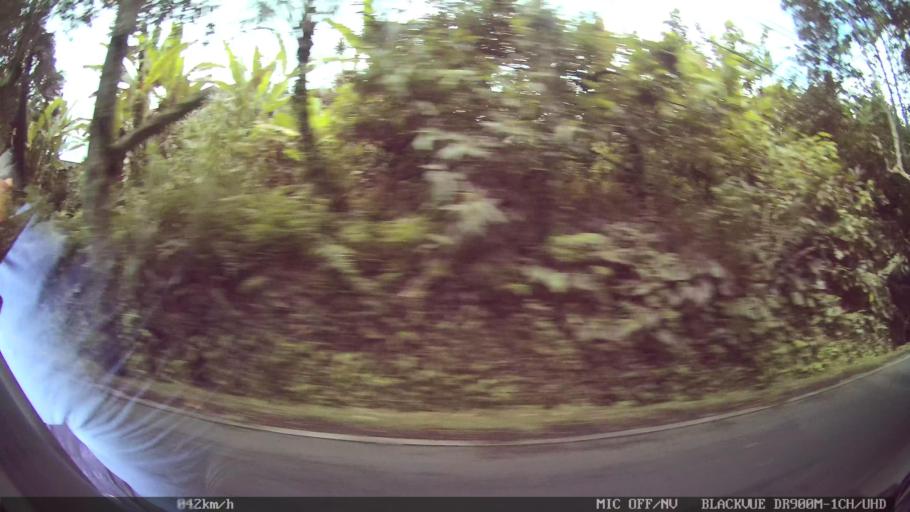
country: ID
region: Bali
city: Petang
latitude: -8.3856
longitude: 115.2203
